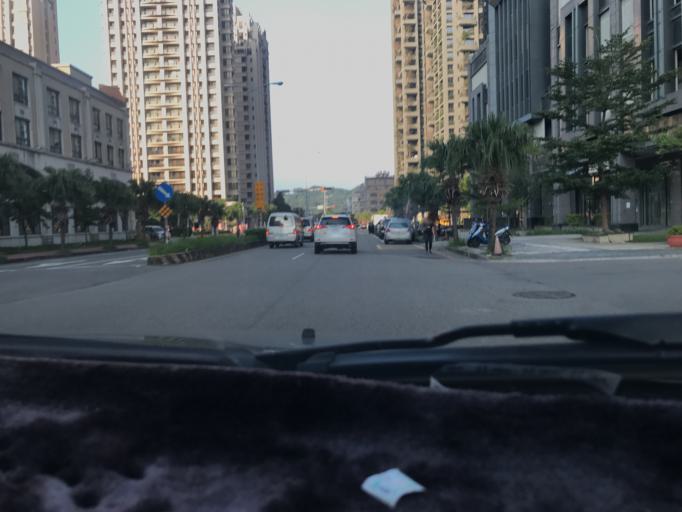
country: TW
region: Taiwan
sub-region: Hsinchu
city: Zhubei
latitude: 24.8116
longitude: 121.0348
